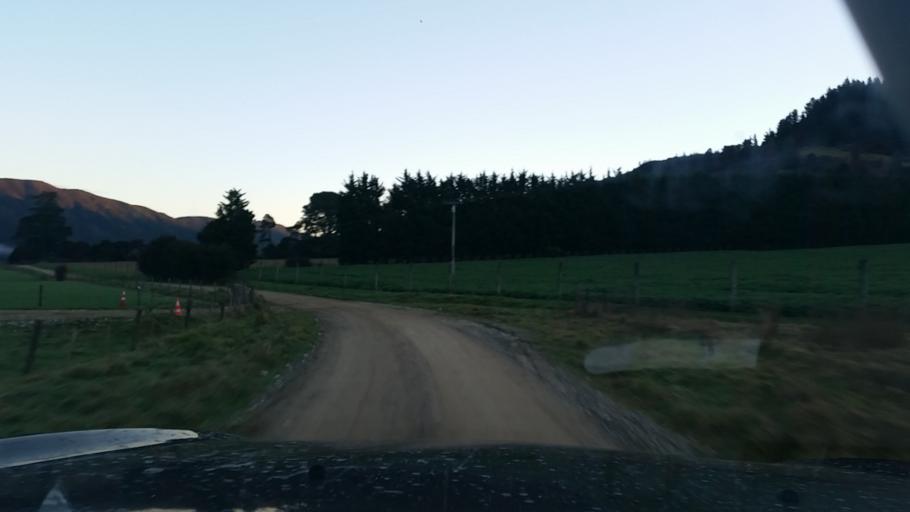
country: NZ
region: Marlborough
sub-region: Marlborough District
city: Picton
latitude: -41.1457
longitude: 174.1341
